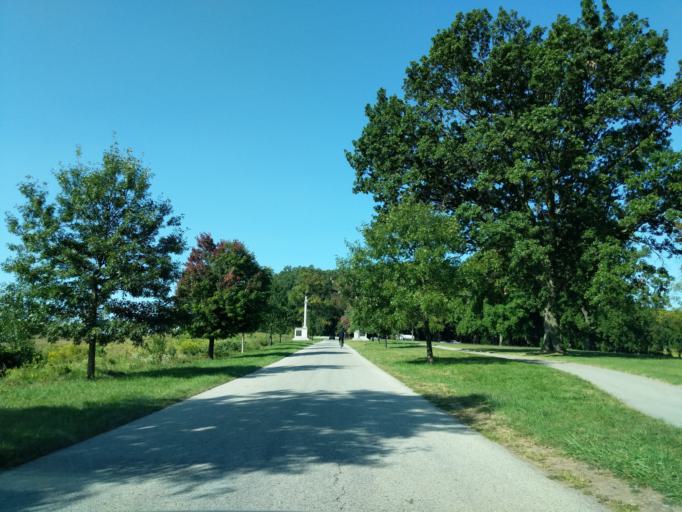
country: US
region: Pennsylvania
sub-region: Chester County
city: Chesterbrook
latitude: 40.0887
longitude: -75.4373
